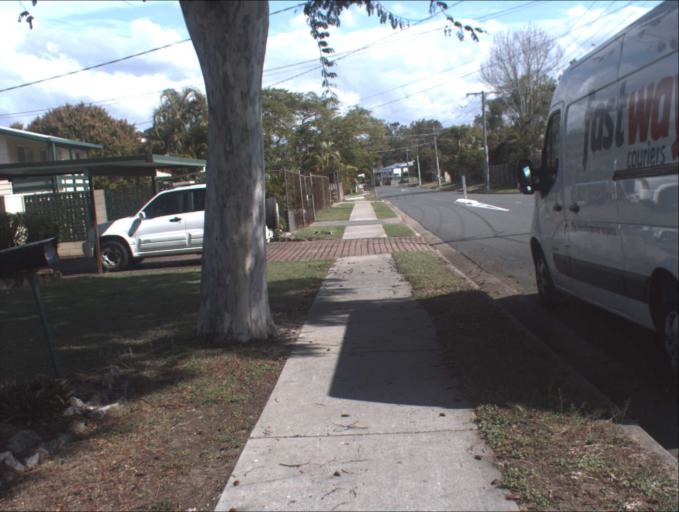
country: AU
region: Queensland
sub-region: Logan
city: Park Ridge South
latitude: -27.6888
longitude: 153.0118
